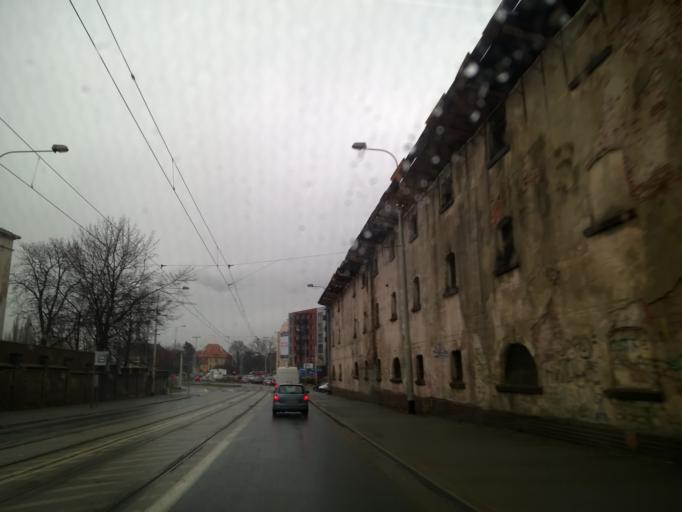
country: PL
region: Lower Silesian Voivodeship
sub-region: Powiat wroclawski
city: Wroclaw
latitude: 51.1149
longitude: 17.0243
